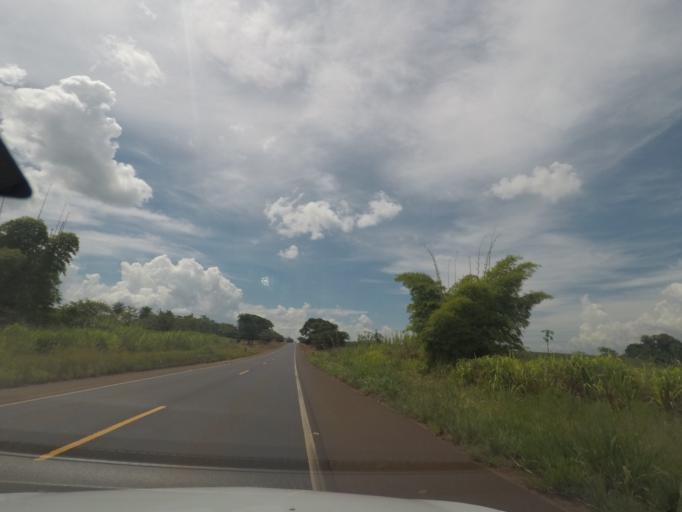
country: BR
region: Sao Paulo
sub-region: Barretos
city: Barretos
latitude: -20.2863
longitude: -48.6703
